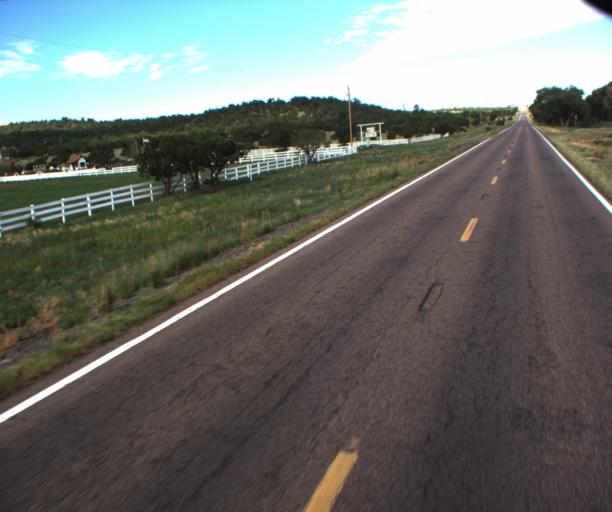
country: US
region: Arizona
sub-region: Navajo County
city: Pinetop-Lakeside
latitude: 34.2716
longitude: -109.6724
